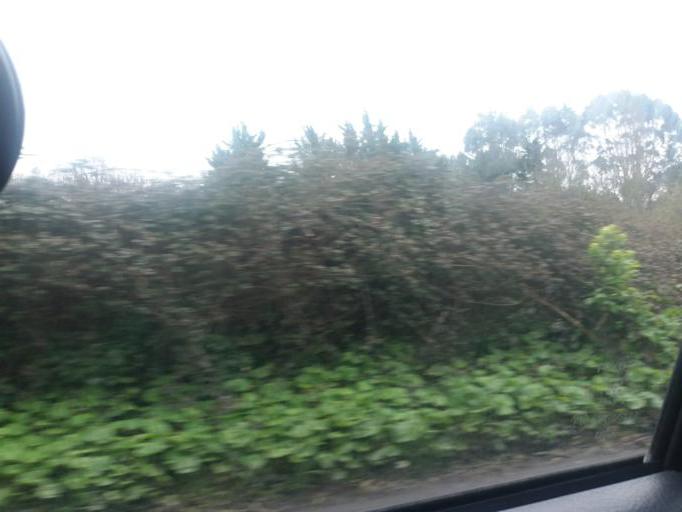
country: IE
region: Leinster
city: Portmarnock
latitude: 53.4273
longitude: -6.1546
